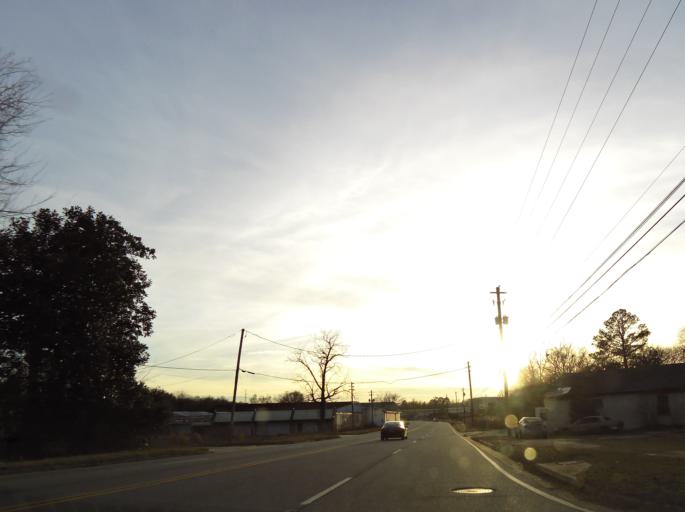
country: US
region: Georgia
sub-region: Bibb County
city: Macon
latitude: 32.7930
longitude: -83.6473
